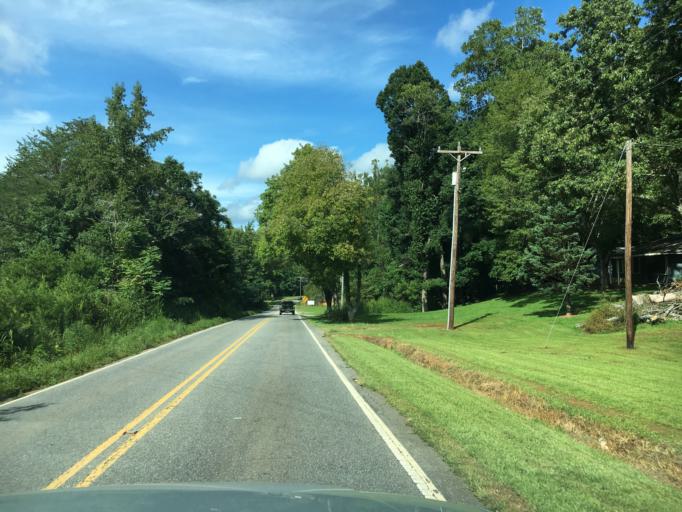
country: US
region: North Carolina
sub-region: Polk County
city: Columbus
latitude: 35.2859
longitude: -82.1770
